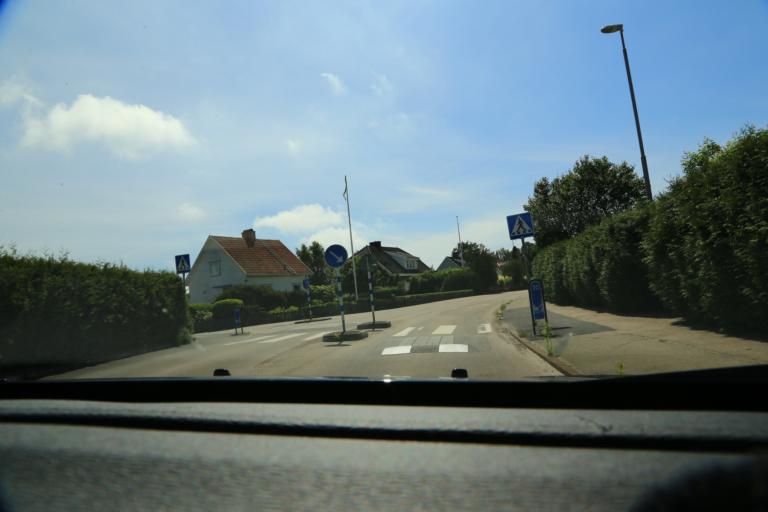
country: SE
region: Halland
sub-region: Varbergs Kommun
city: Varberg
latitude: 57.1049
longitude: 12.2905
